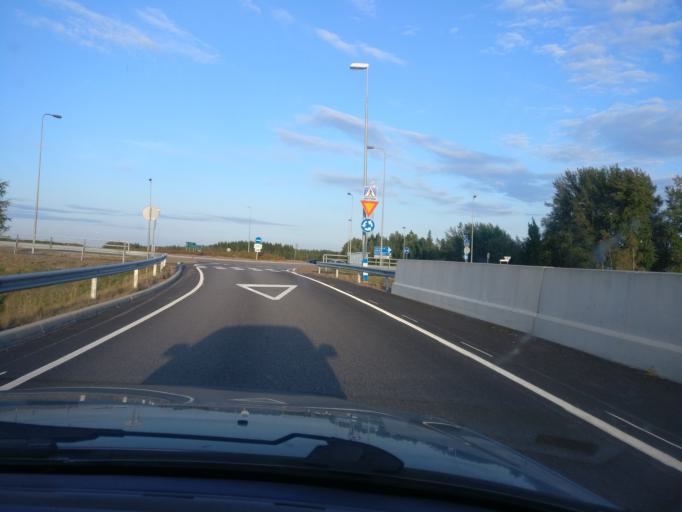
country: FI
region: Kymenlaakso
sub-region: Kotka-Hamina
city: Broby
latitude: 60.5029
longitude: 26.7413
